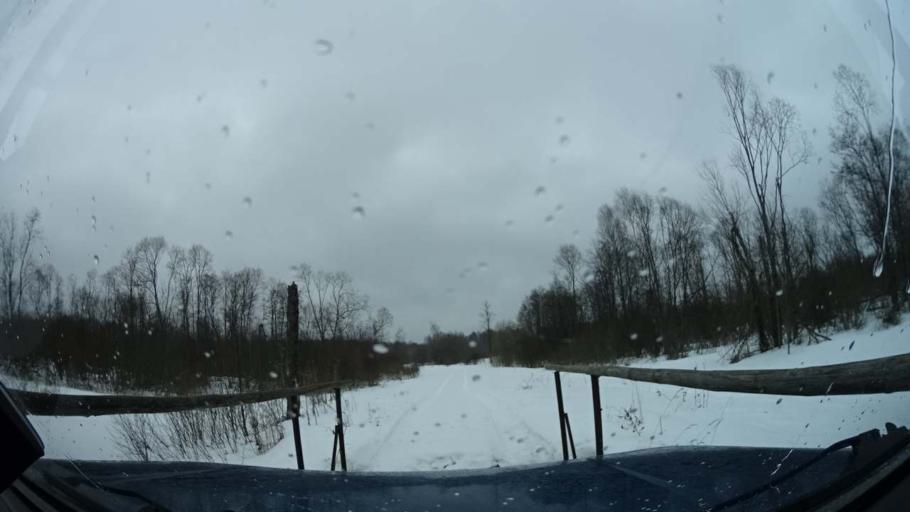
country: RU
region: Tverskaya
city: Gorodnya
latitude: 56.8316
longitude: 36.4024
